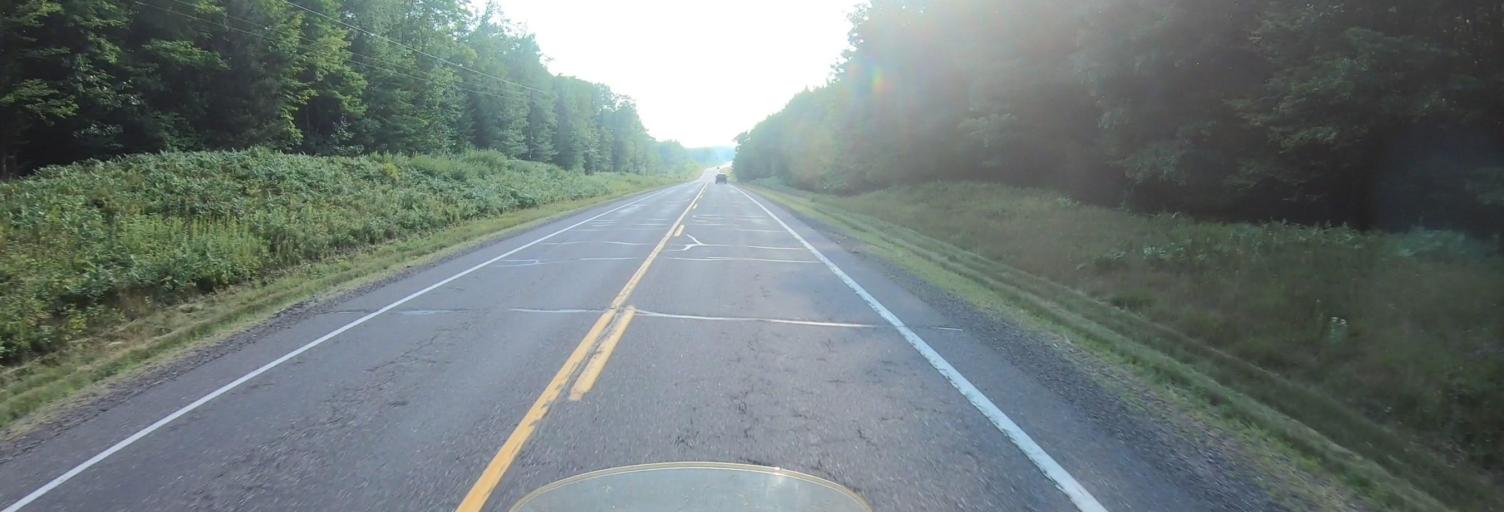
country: US
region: Wisconsin
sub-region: Sawyer County
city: Little Round Lake
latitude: 46.0704
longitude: -91.1074
